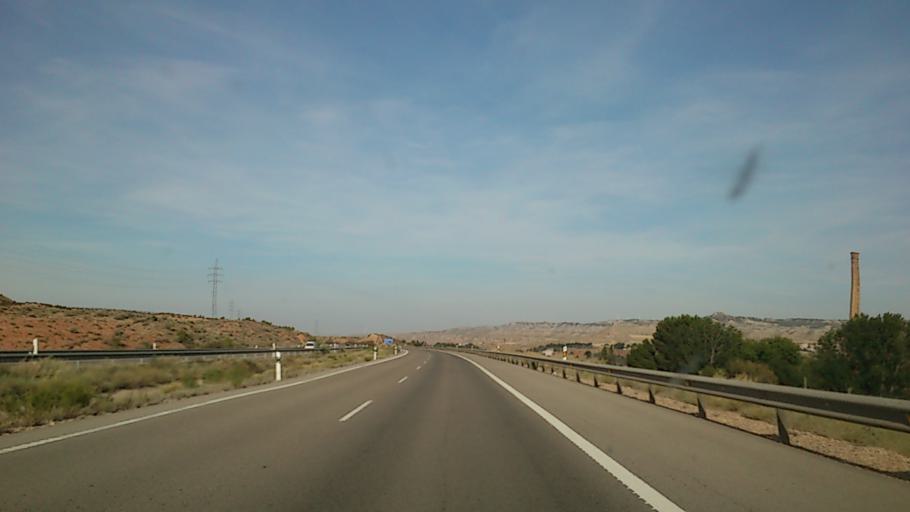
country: ES
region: Aragon
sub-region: Provincia de Zaragoza
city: Botorrita
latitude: 41.5030
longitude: -1.0532
